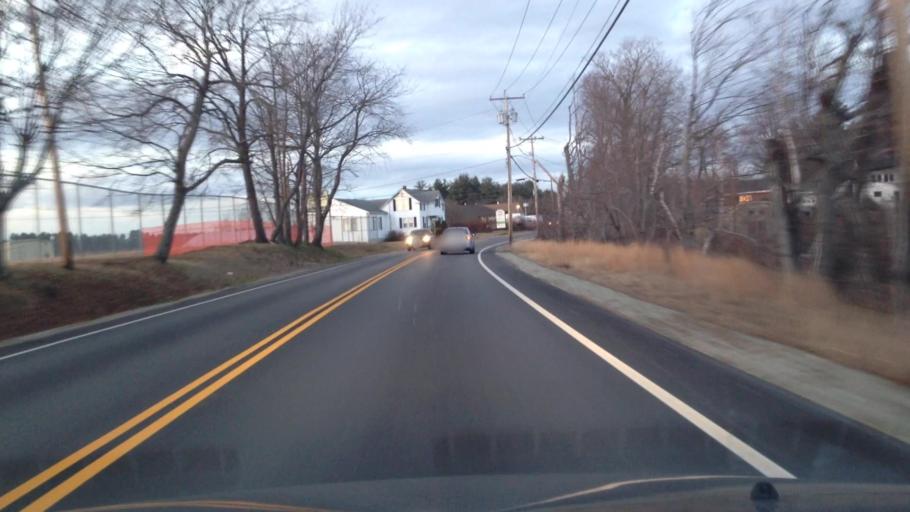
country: US
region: New Hampshire
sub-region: Cheshire County
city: Keene
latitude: 42.9010
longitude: -72.2651
